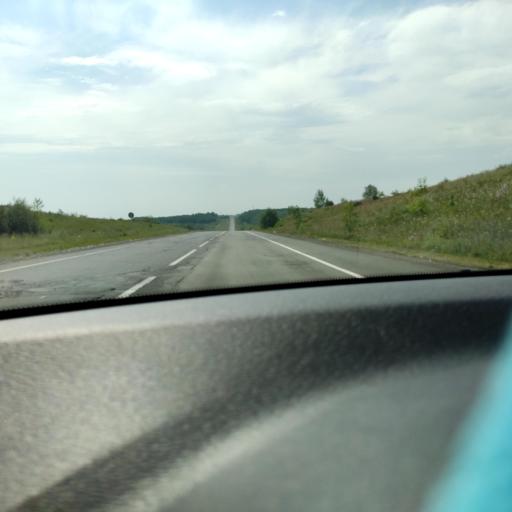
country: RU
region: Samara
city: Petra-Dubrava
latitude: 53.2984
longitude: 50.4038
